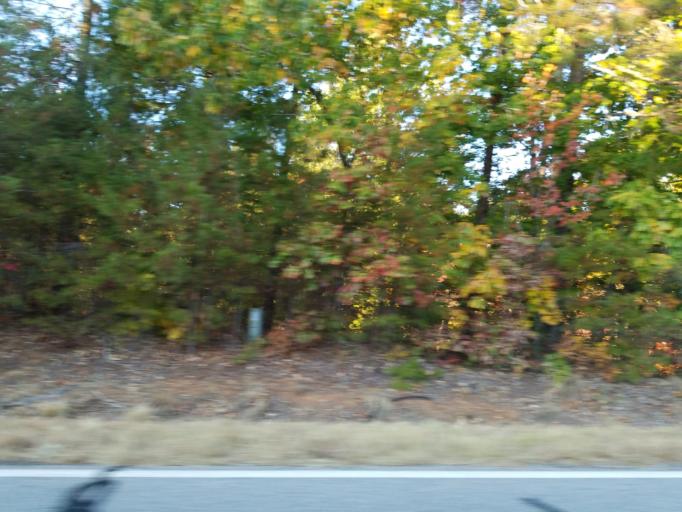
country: US
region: Georgia
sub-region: Dawson County
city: Dawsonville
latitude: 34.5469
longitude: -84.1231
